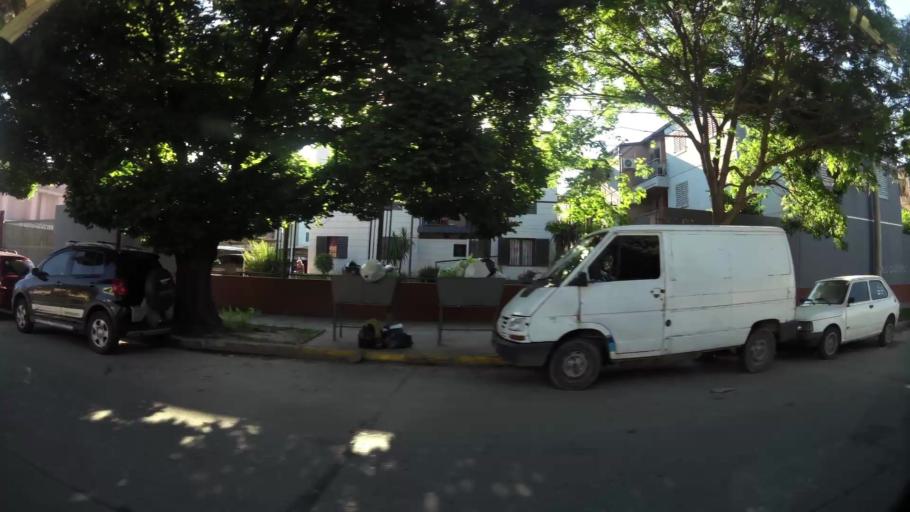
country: AR
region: Cordoba
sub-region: Departamento de Capital
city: Cordoba
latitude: -31.3846
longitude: -64.1893
